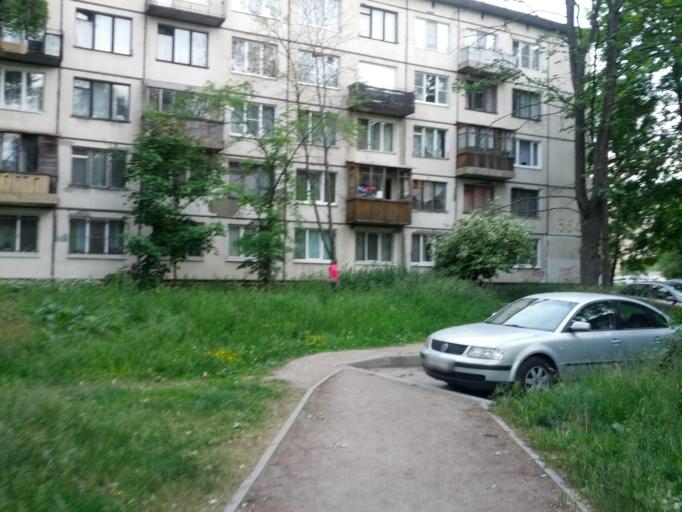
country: RU
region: St.-Petersburg
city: Obukhovo
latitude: 59.8938
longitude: 30.4753
